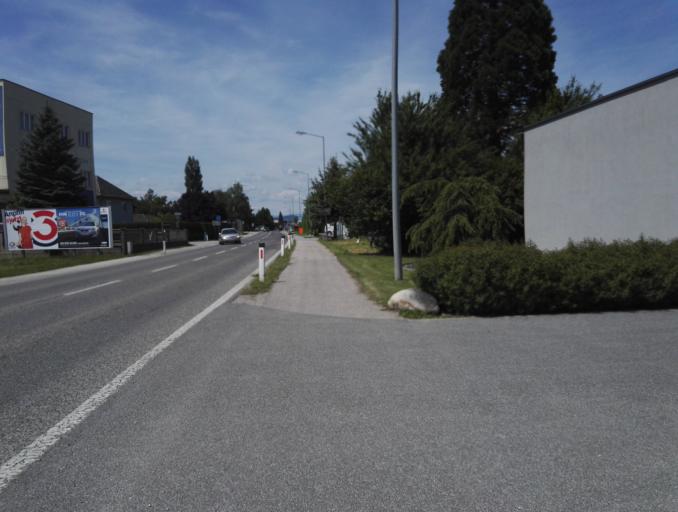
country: AT
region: Styria
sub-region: Politischer Bezirk Graz-Umgebung
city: Gossendorf
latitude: 46.9845
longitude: 15.4613
